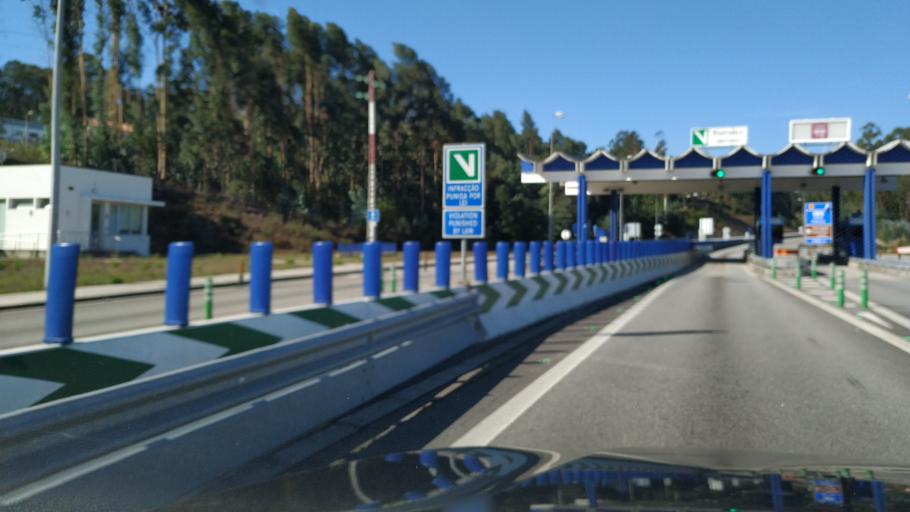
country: PT
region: Porto
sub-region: Vila Nova de Gaia
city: Sandim
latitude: 41.0477
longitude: -8.5034
